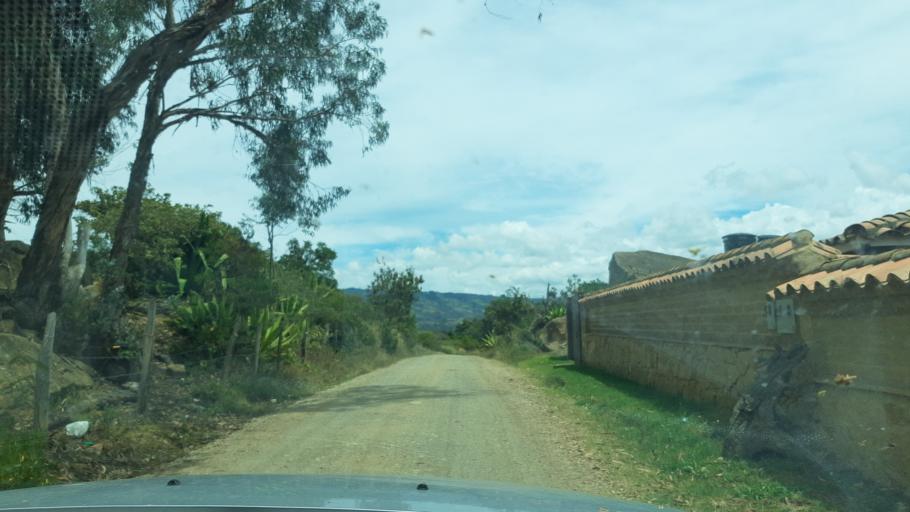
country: CO
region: Boyaca
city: Santa Sofia
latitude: 5.6833
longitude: -73.5914
